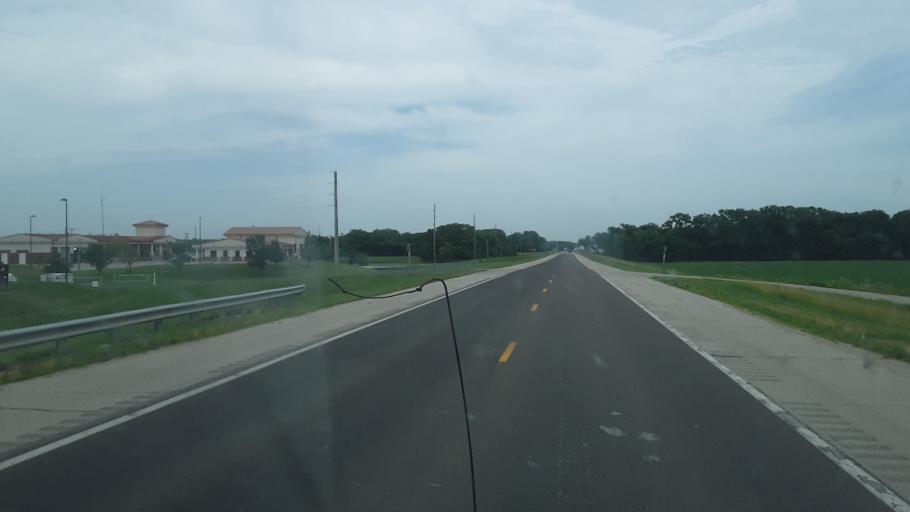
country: US
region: Kansas
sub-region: Allen County
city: Iola
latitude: 37.9220
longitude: -95.4259
